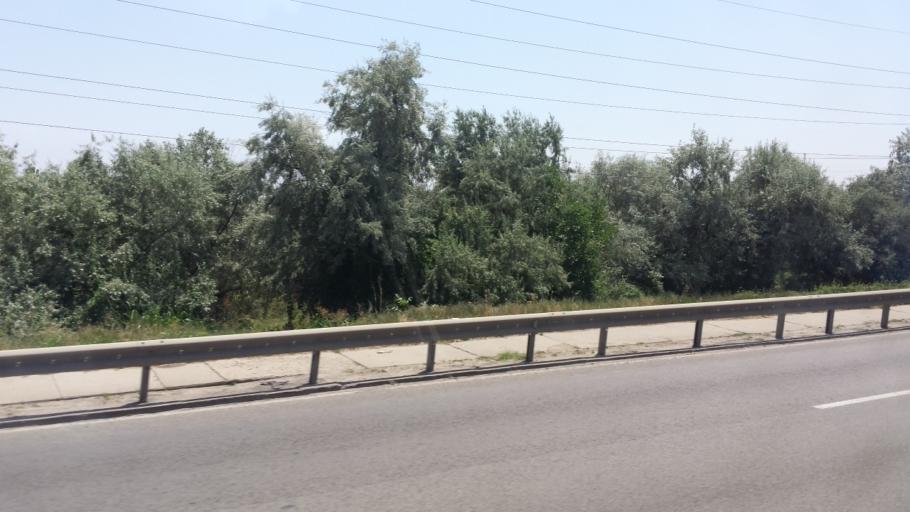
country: RO
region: Constanta
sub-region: Comuna Ovidiu
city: Ovidiu
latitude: 44.2656
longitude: 28.5550
